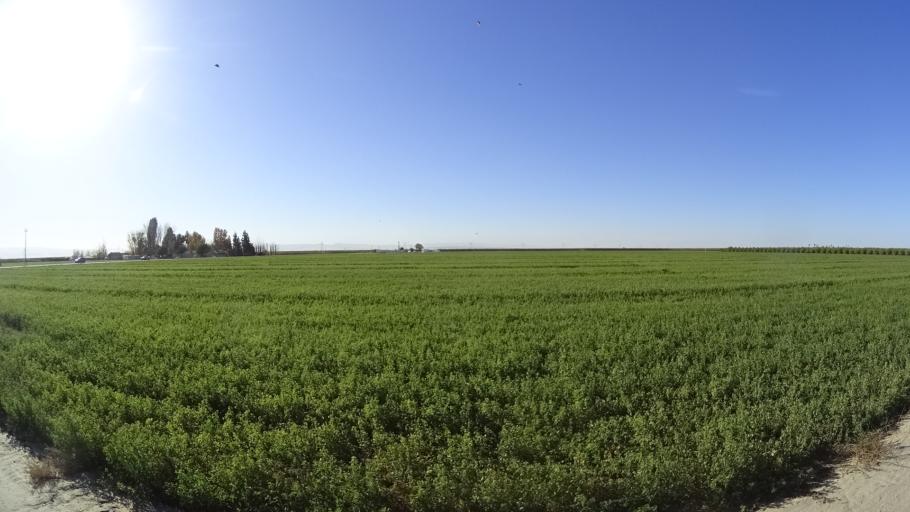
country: US
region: California
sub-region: Kern County
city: Greenacres
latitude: 35.2683
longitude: -119.1183
